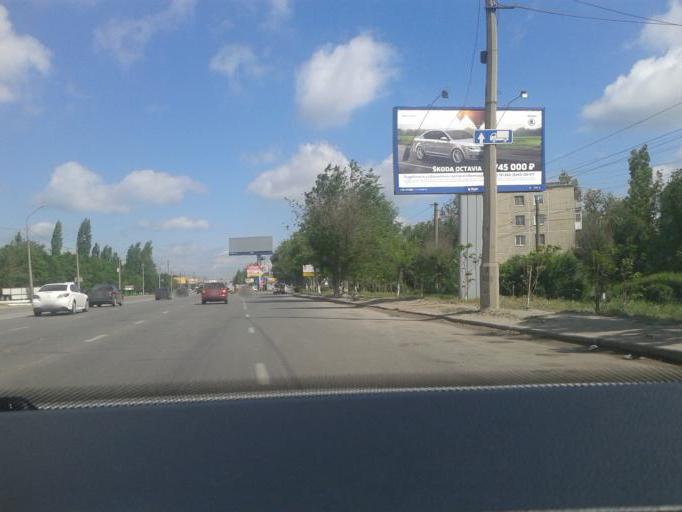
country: RU
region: Volgograd
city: Volgograd
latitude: 48.7585
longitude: 44.4794
